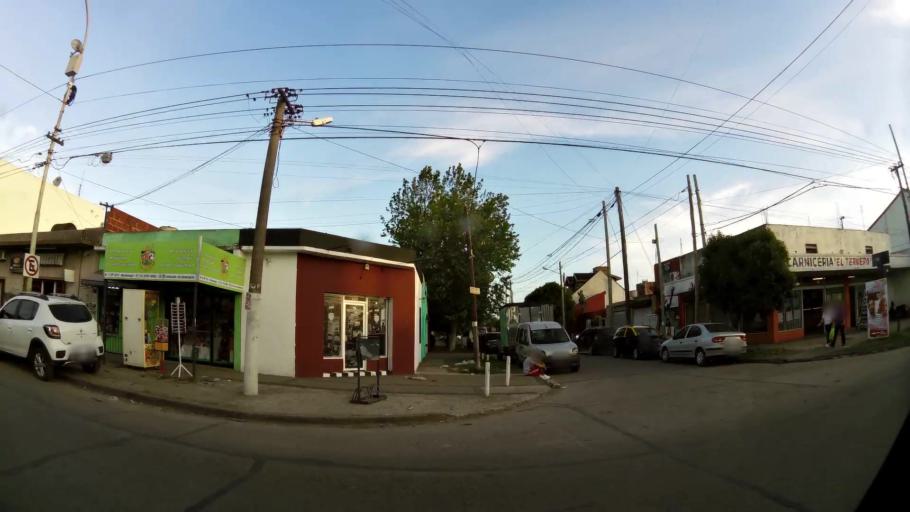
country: AR
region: Buenos Aires
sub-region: Partido de Quilmes
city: Quilmes
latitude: -34.7752
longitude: -58.2348
